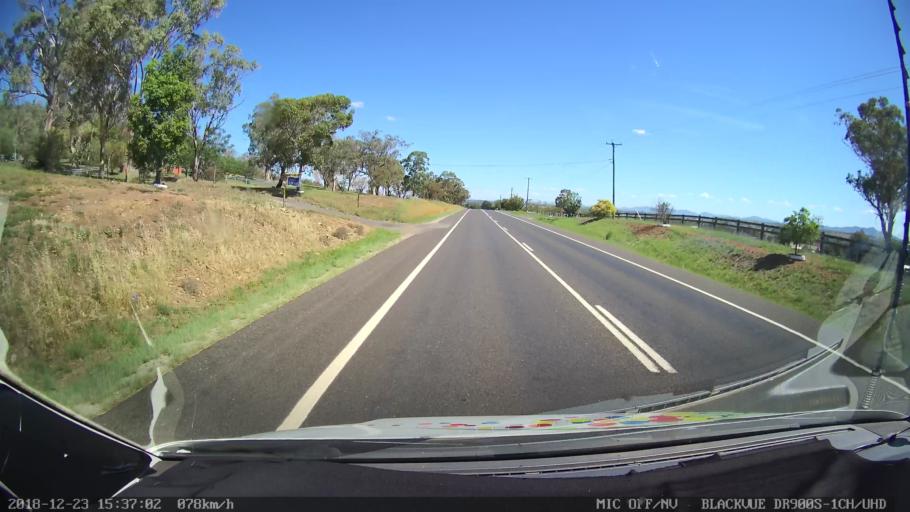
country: AU
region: New South Wales
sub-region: Tamworth Municipality
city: Tamworth
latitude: -31.0478
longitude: 150.8887
